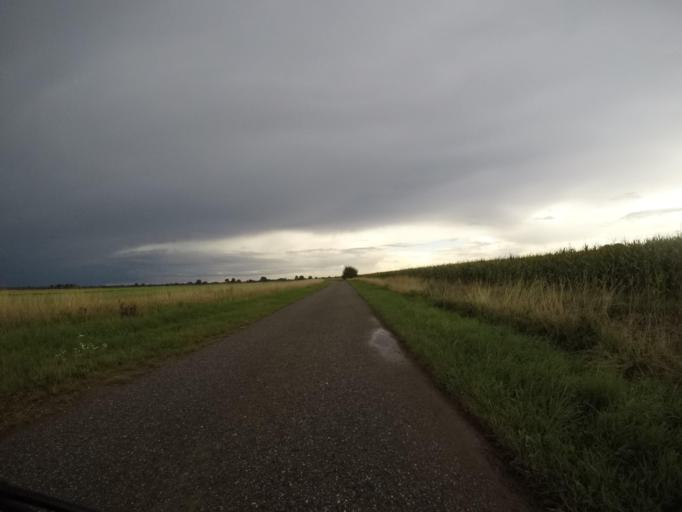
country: DE
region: Lower Saxony
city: Neu Darchau
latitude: 53.2520
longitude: 10.9003
